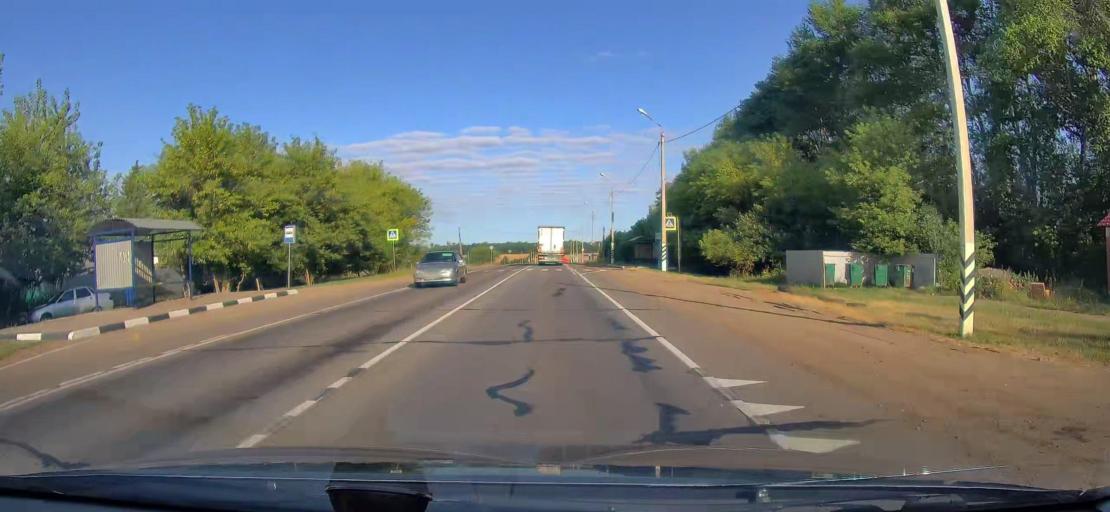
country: RU
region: Tula
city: Bol'shoye Skuratovo
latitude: 53.4535
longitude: 36.8754
